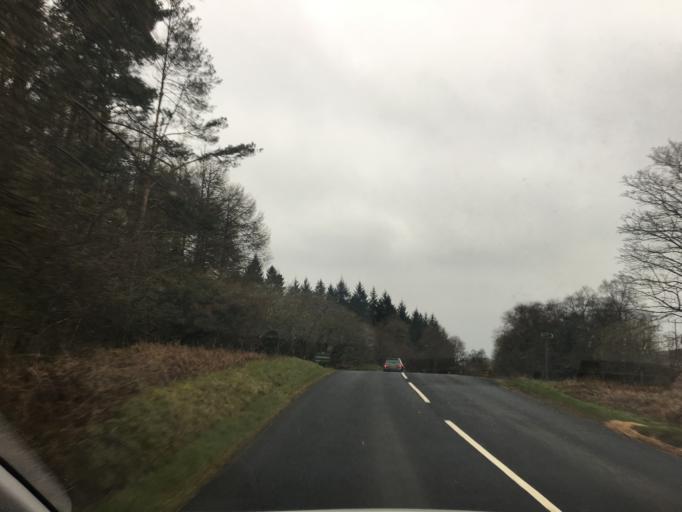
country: GB
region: Scotland
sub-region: North Ayrshire
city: Lamlash
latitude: 55.5526
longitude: -5.1428
